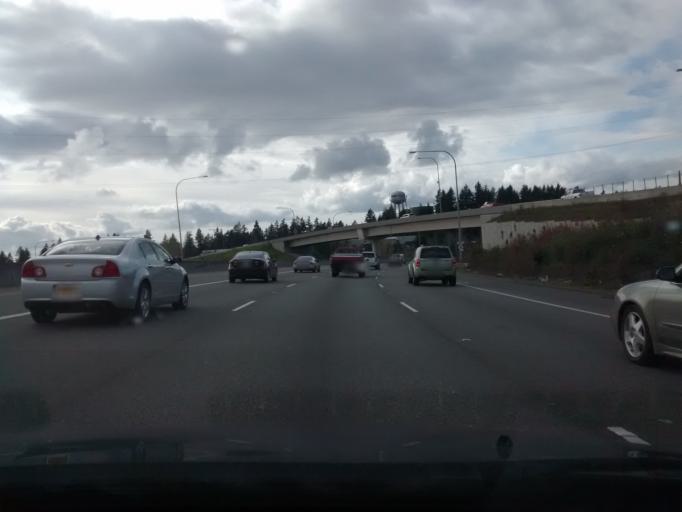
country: US
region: Washington
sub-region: Pierce County
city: Fircrest
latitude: 47.2351
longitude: -122.4968
